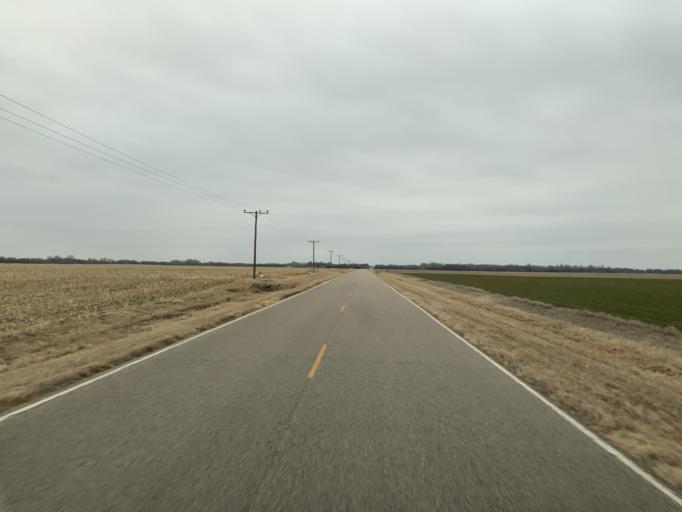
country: US
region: Kansas
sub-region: Reno County
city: South Hutchinson
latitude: 37.9544
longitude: -98.0876
